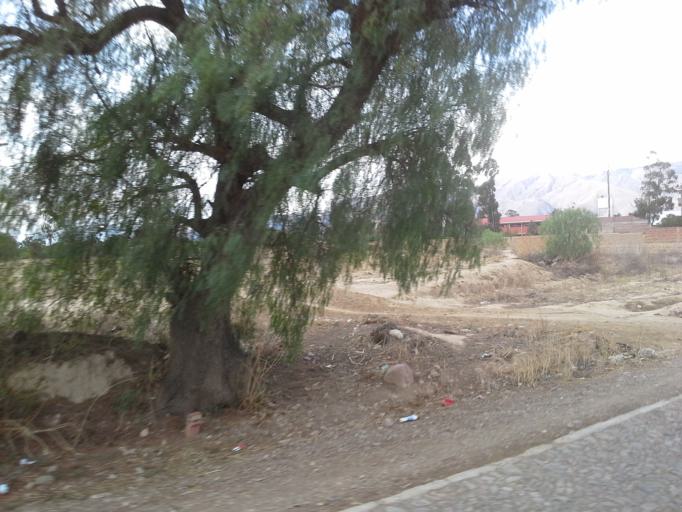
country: BO
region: Cochabamba
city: Tarata
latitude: -17.5873
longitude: -66.0181
